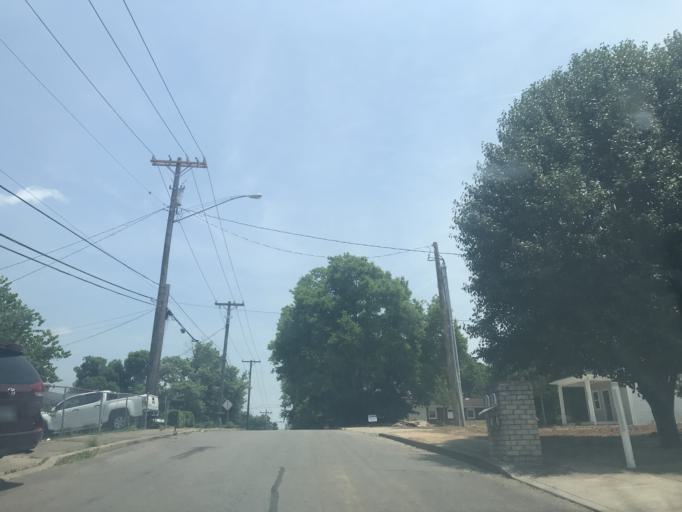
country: US
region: Tennessee
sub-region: Davidson County
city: Nashville
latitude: 36.1900
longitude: -86.8120
